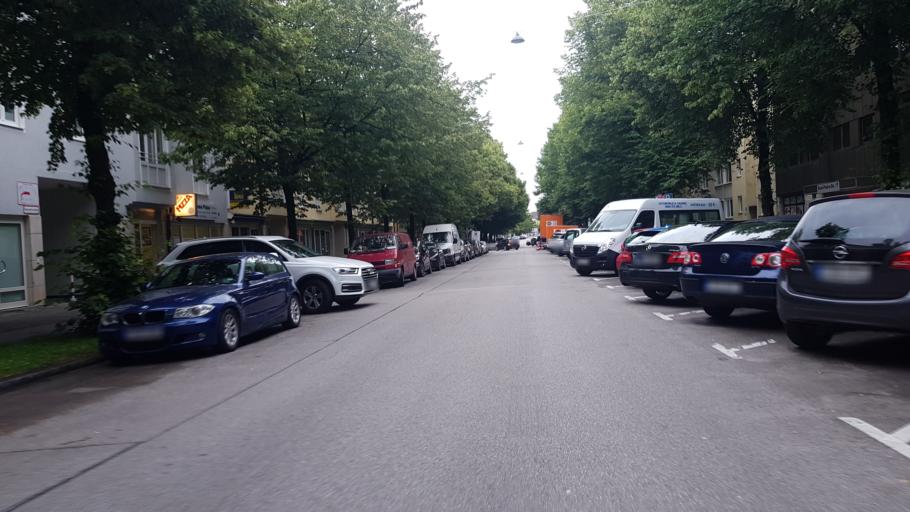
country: DE
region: Bavaria
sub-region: Upper Bavaria
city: Munich
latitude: 48.1596
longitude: 11.5419
